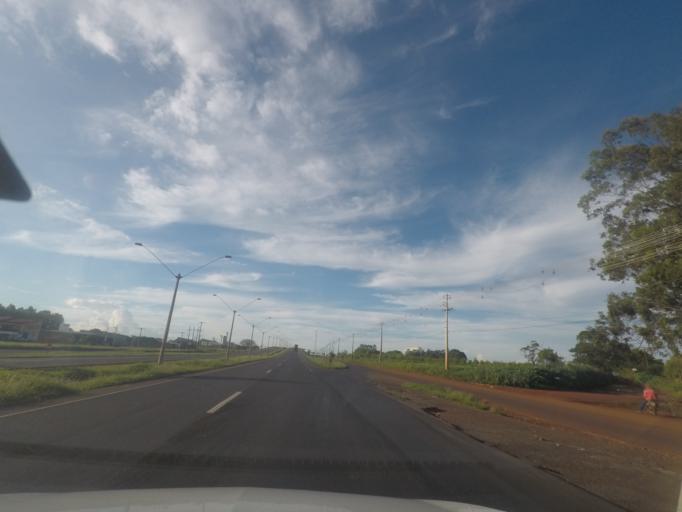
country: BR
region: Goias
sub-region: Itumbiara
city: Itumbiara
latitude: -18.3632
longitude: -49.2149
